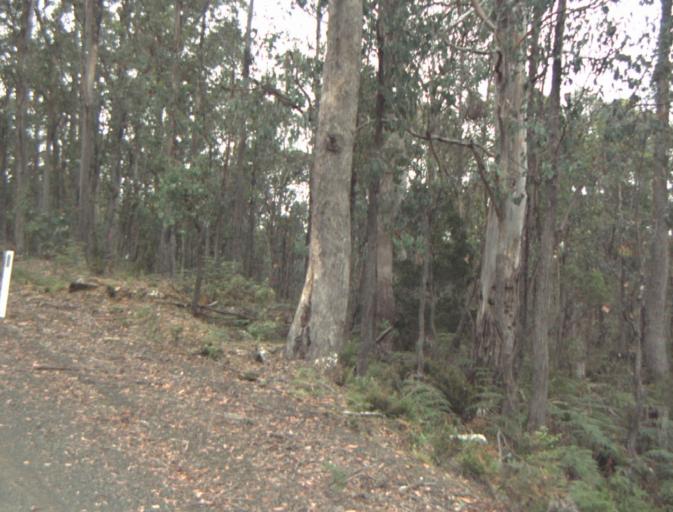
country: AU
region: Tasmania
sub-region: Dorset
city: Scottsdale
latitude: -41.4992
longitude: 147.6030
